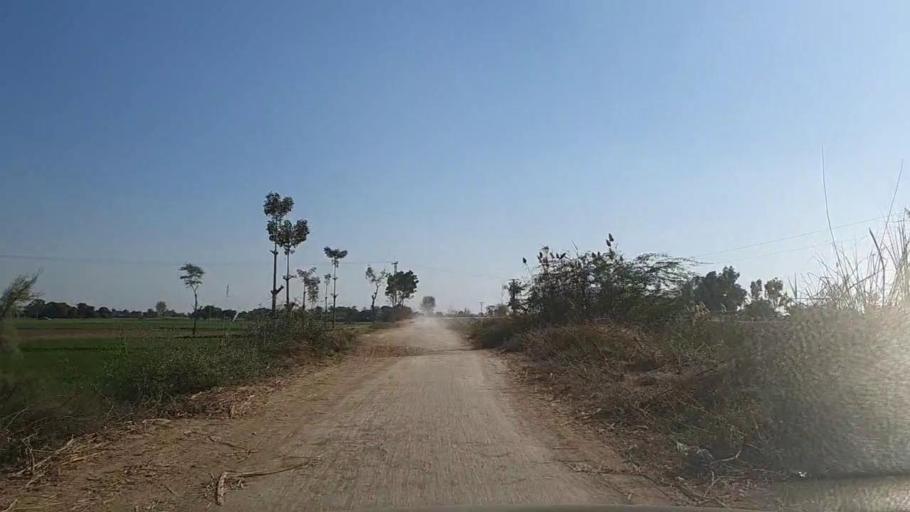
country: PK
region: Sindh
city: Nawabshah
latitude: 26.2259
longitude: 68.4287
